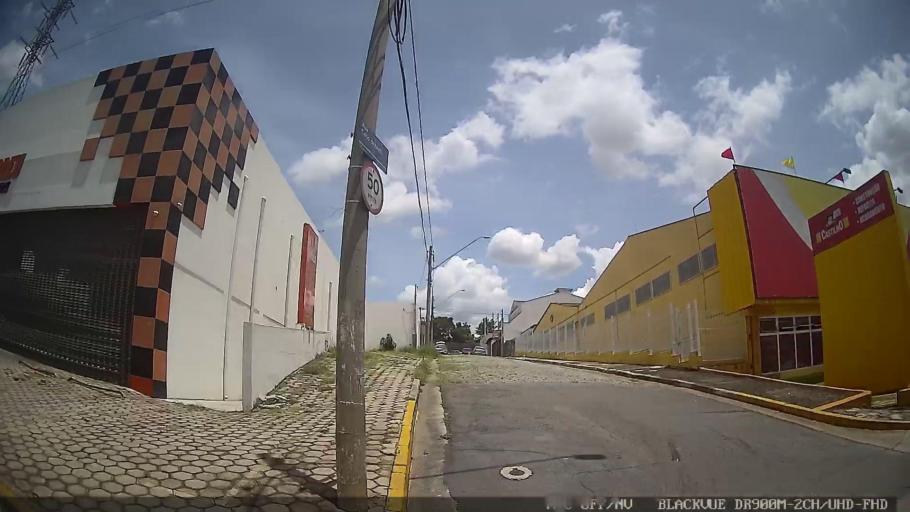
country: BR
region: Sao Paulo
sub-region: Mogi das Cruzes
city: Mogi das Cruzes
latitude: -23.5332
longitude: -46.2105
